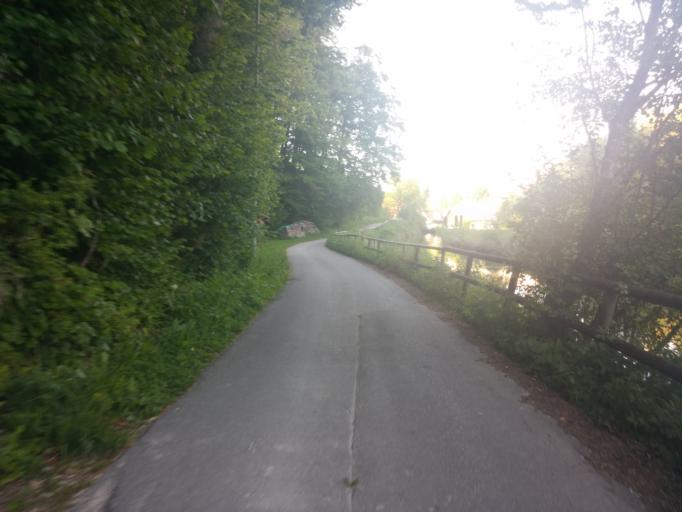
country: DE
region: Bavaria
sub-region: Swabia
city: Lautrach
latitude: 47.8970
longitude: 10.1117
